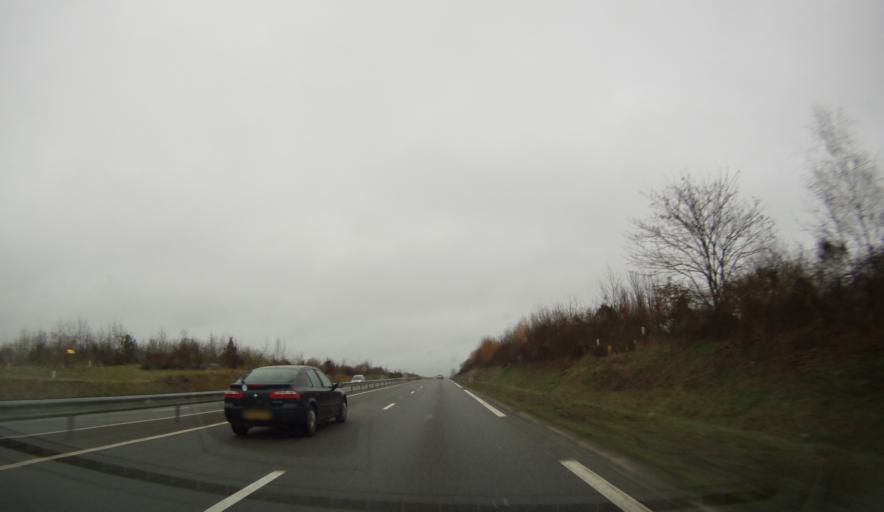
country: FR
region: Brittany
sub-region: Departement d'Ille-et-Vilaine
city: Saint-Armel
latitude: 48.0051
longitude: -1.5951
